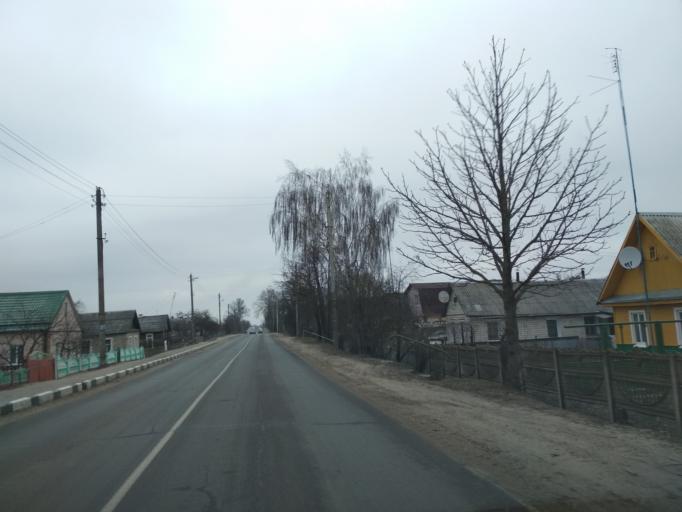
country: BY
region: Minsk
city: Mar''ina Horka
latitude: 53.4985
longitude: 28.1479
